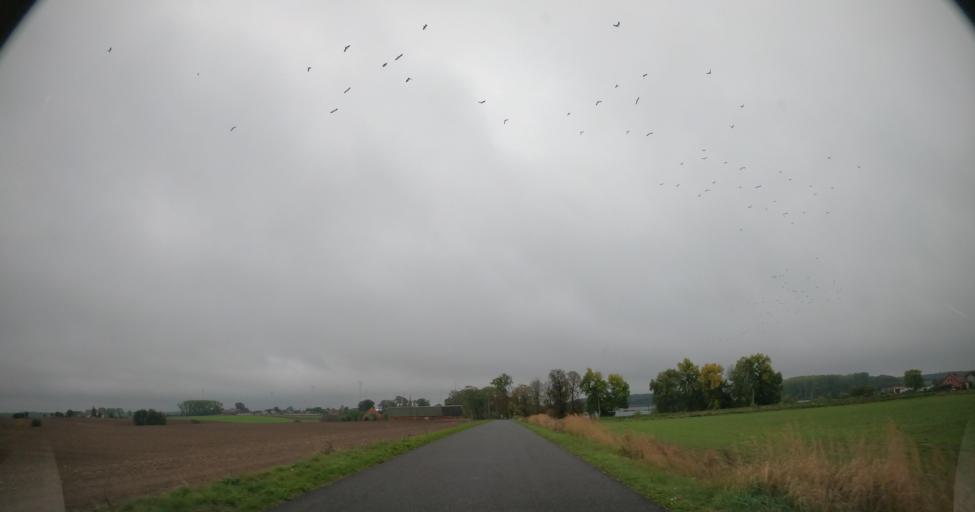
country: PL
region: West Pomeranian Voivodeship
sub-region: Powiat pyrzycki
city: Kozielice
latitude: 53.0993
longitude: 14.7664
